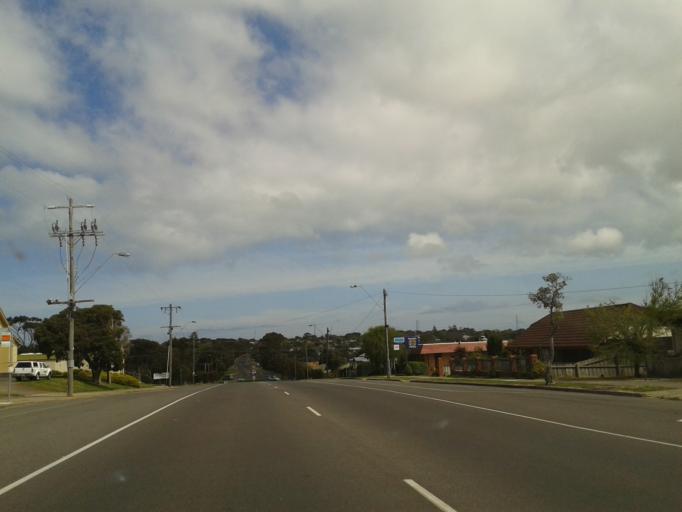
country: AU
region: Victoria
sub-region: Glenelg
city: Portland
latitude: -38.3514
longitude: 141.6062
